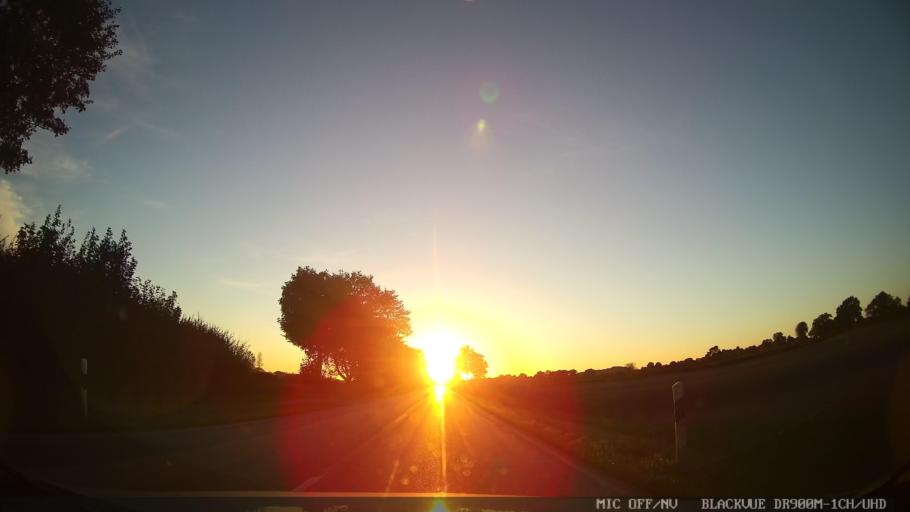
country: DE
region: Schleswig-Holstein
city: Sierksdorf
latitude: 54.0937
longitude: 10.7676
